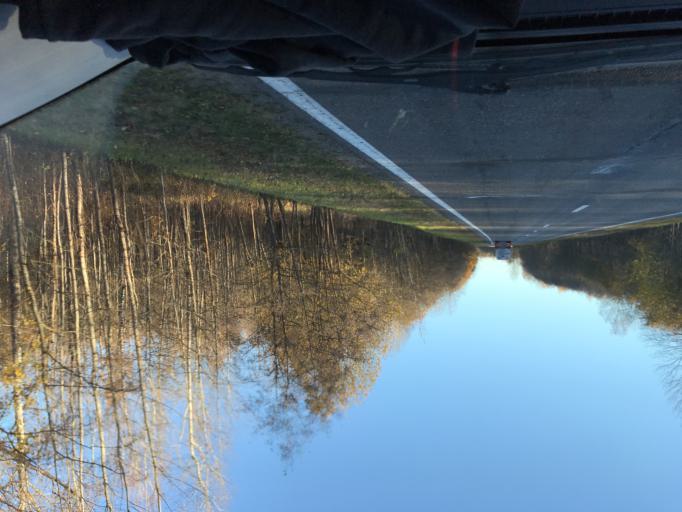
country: BY
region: Vitebsk
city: Vitebsk
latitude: 55.3584
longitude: 30.1769
